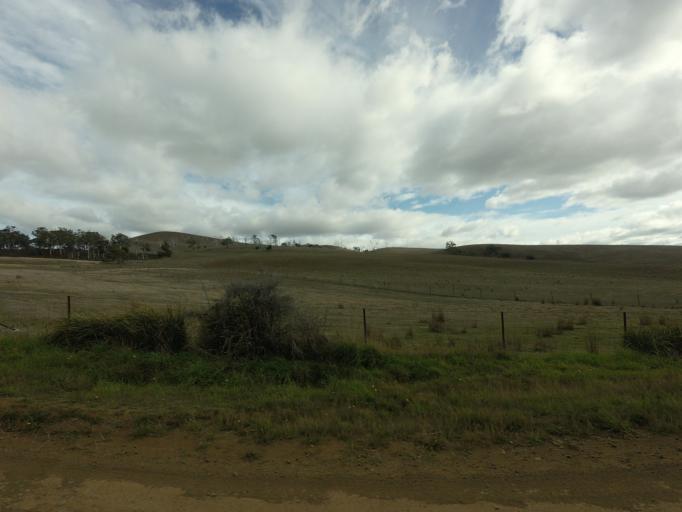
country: AU
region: Tasmania
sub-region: Brighton
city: Bridgewater
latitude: -42.4746
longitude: 147.2916
